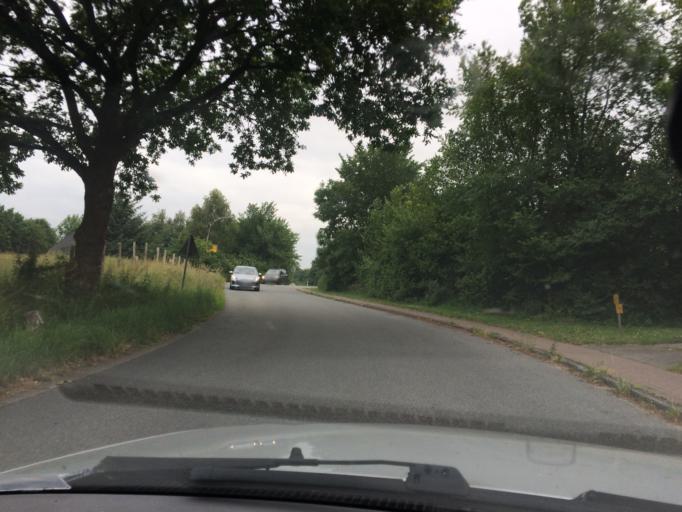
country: DE
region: Schleswig-Holstein
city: Oeversee
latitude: 54.6922
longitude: 9.4310
